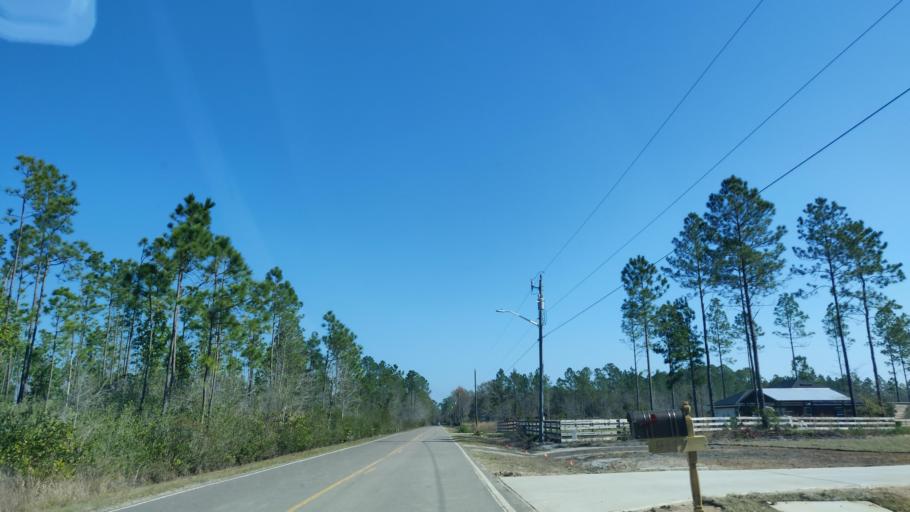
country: US
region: Florida
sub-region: Duval County
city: Baldwin
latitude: 30.1881
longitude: -81.9697
